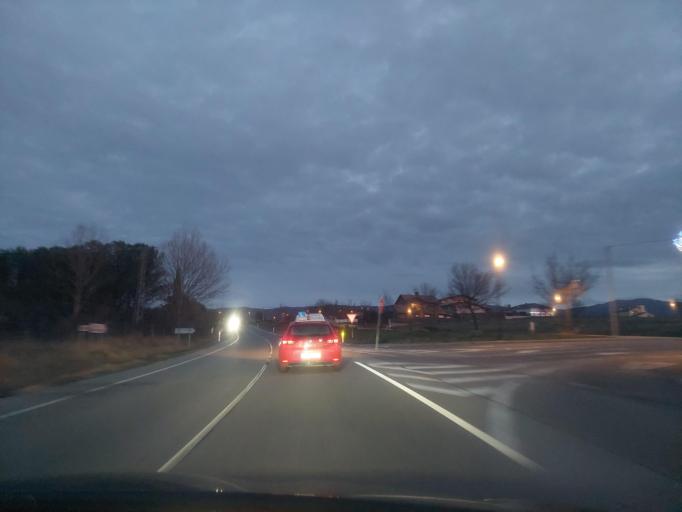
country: ES
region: Castille and Leon
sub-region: Provincia de Segovia
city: La Lastrilla
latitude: 40.9521
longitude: -4.0974
